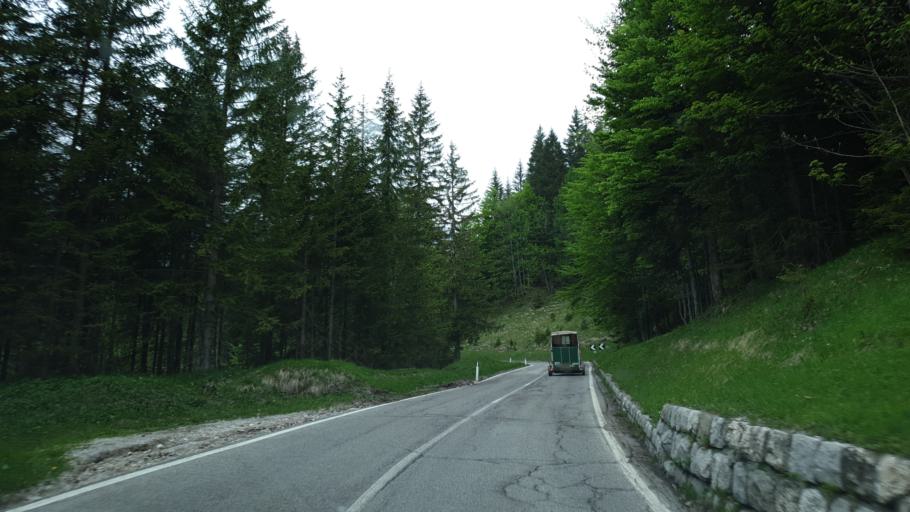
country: IT
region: Veneto
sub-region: Provincia di Belluno
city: San Vito
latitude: 46.5551
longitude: 12.2472
